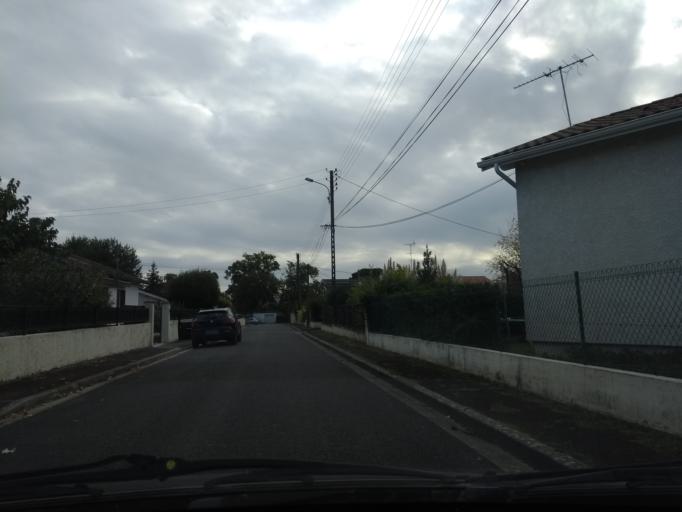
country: FR
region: Aquitaine
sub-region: Departement de la Gironde
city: Gradignan
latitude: 44.7809
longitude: -0.6139
